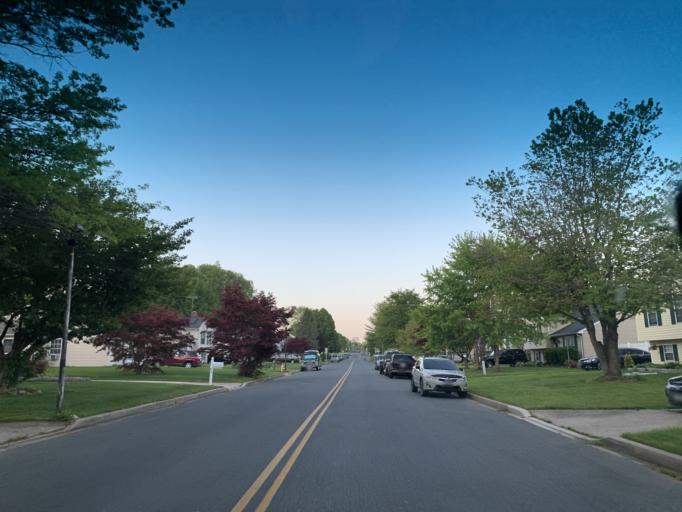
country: US
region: Maryland
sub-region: Harford County
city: Aberdeen
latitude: 39.5008
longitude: -76.1837
